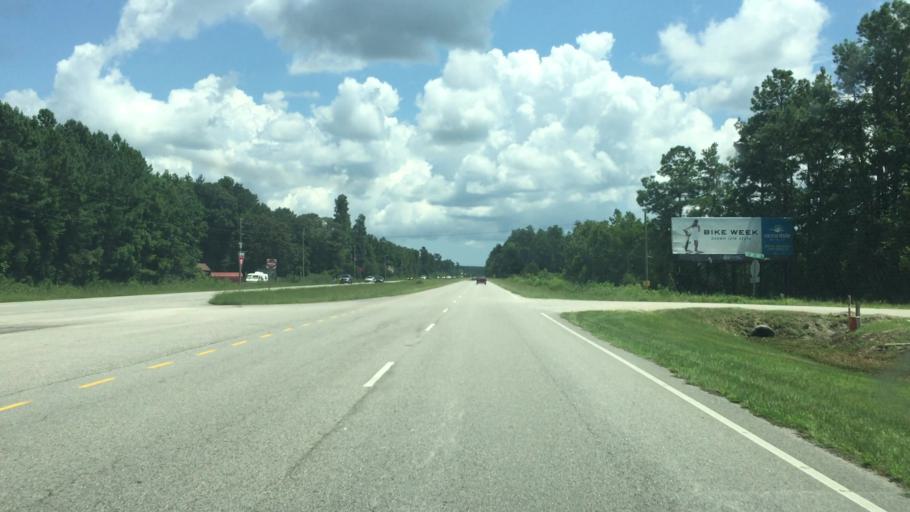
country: US
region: South Carolina
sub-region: Horry County
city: Loris
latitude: 34.0145
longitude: -78.7847
